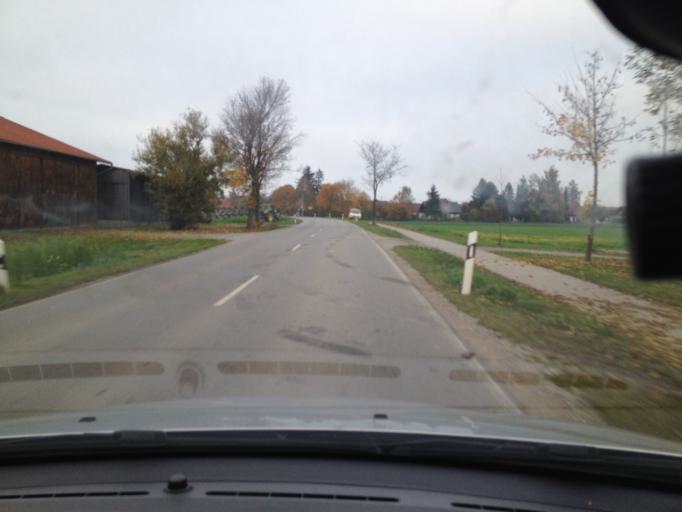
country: DE
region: Bavaria
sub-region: Swabia
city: Kleinaitingen
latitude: 48.2131
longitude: 10.8373
